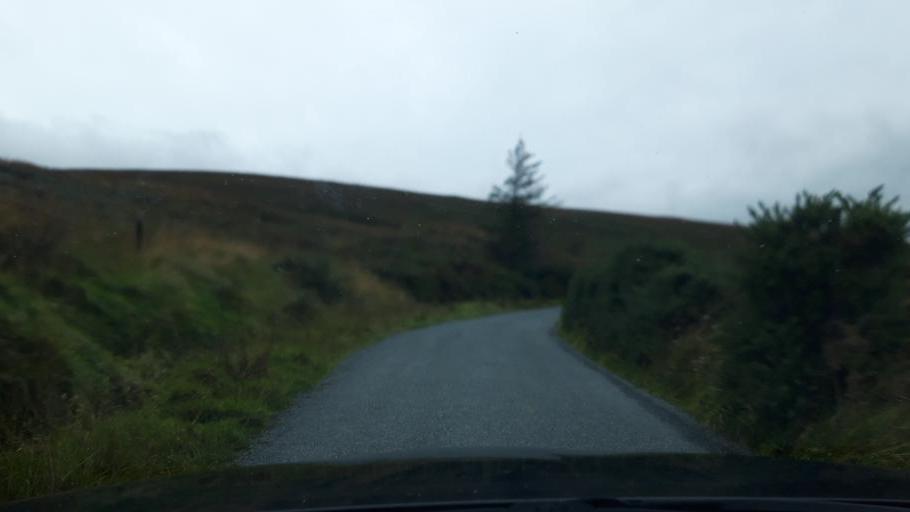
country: IE
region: Leinster
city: Ballinteer
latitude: 53.1909
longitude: -6.2909
